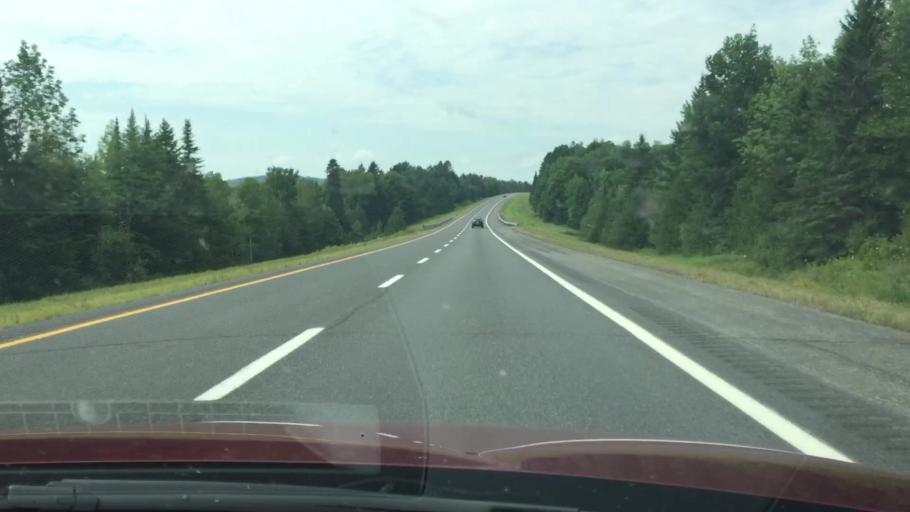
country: US
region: Maine
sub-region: Aroostook County
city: Hodgdon
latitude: 46.1407
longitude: -68.0090
